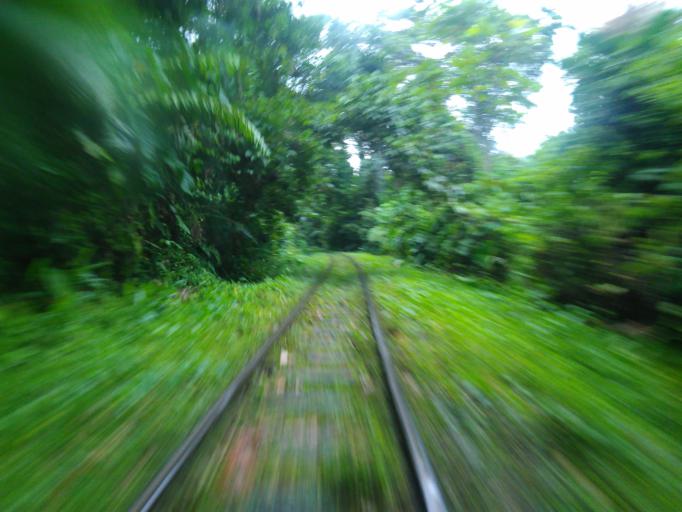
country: CO
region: Valle del Cauca
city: Buenaventura
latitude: 3.8440
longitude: -76.8696
